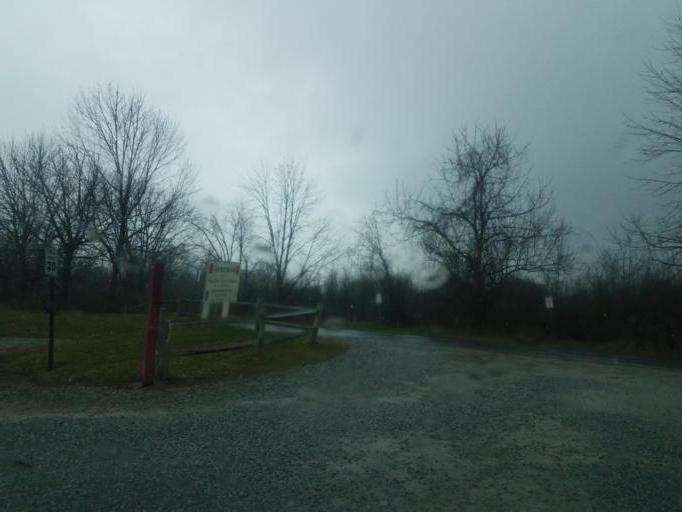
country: US
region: Ohio
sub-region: Delaware County
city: Lewis Center
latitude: 40.1984
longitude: -82.9743
